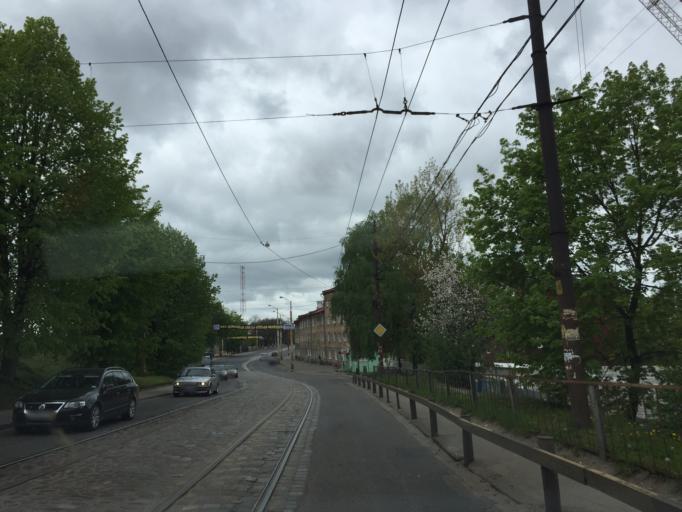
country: RU
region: Kaliningrad
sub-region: Gorod Kaliningrad
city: Kaliningrad
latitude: 54.6954
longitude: 20.4868
